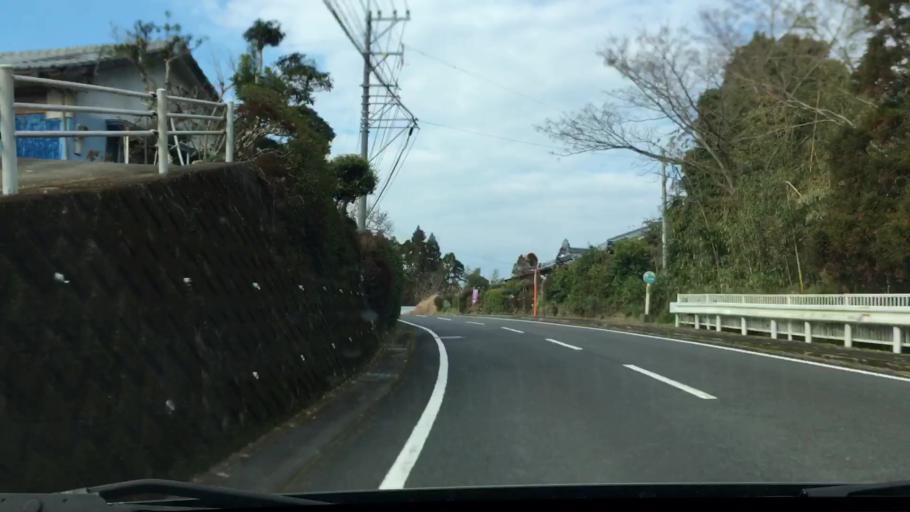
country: JP
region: Miyazaki
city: Kushima
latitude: 31.5402
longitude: 131.2427
